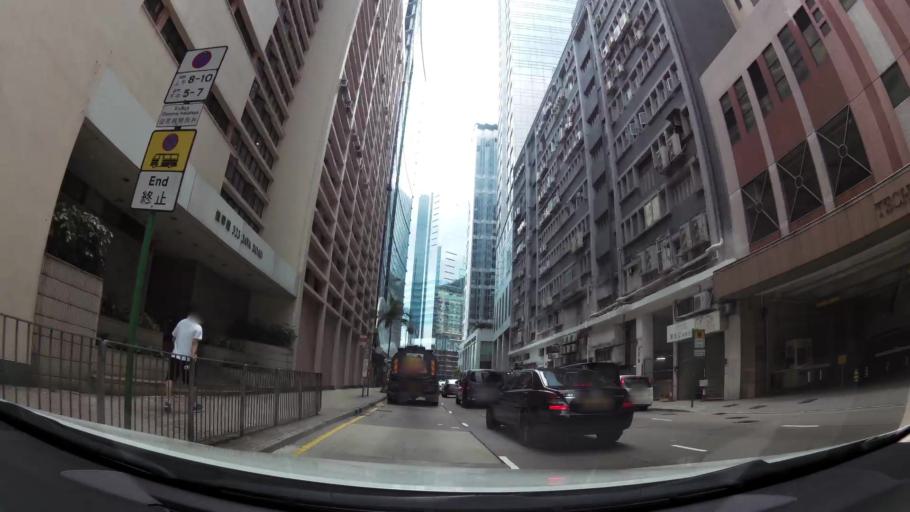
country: HK
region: Kowloon City
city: Kowloon
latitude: 22.2922
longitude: 114.2075
